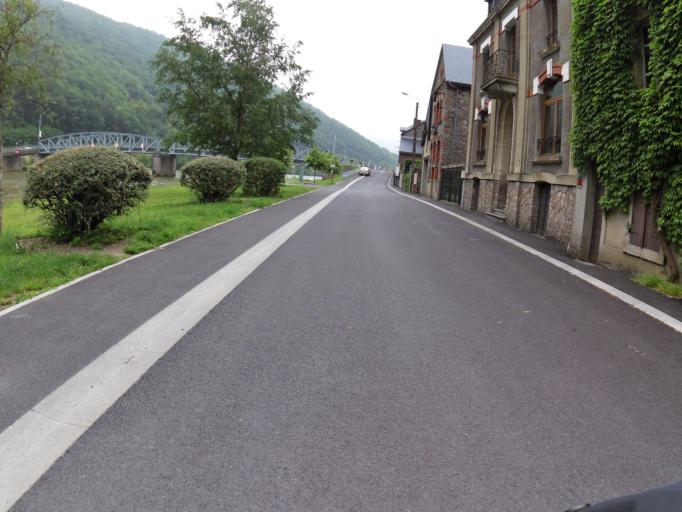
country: FR
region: Champagne-Ardenne
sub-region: Departement des Ardennes
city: Haybes
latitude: 50.0104
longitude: 4.7041
